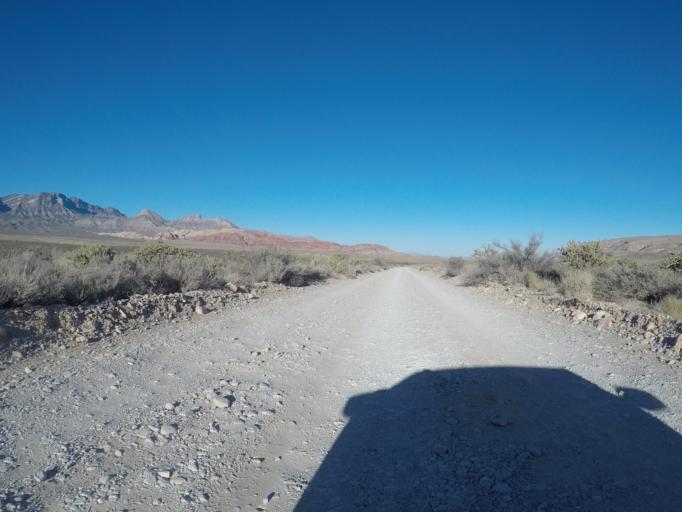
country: US
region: Nevada
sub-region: Clark County
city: Summerlin South
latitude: 36.1121
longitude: -115.4644
